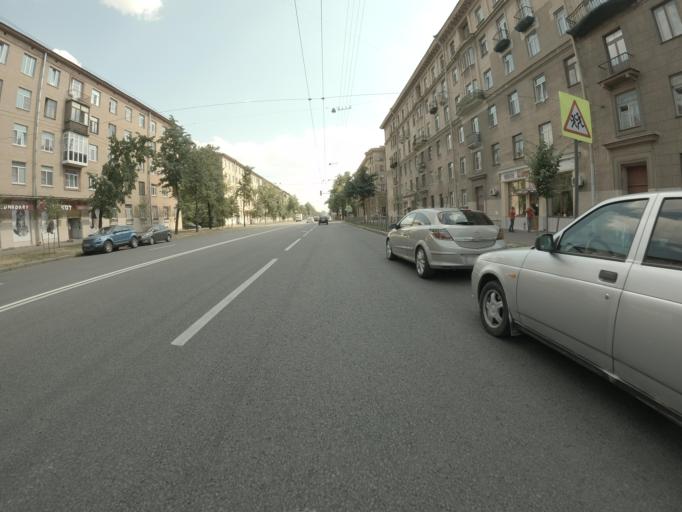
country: RU
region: St.-Petersburg
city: Avtovo
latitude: 59.8712
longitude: 30.2678
